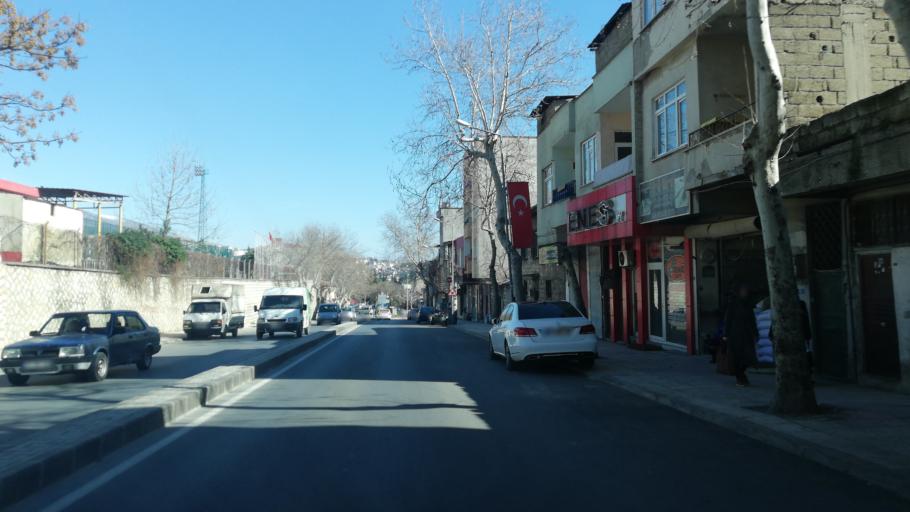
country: TR
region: Kahramanmaras
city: Kahramanmaras
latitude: 37.5885
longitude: 36.9170
